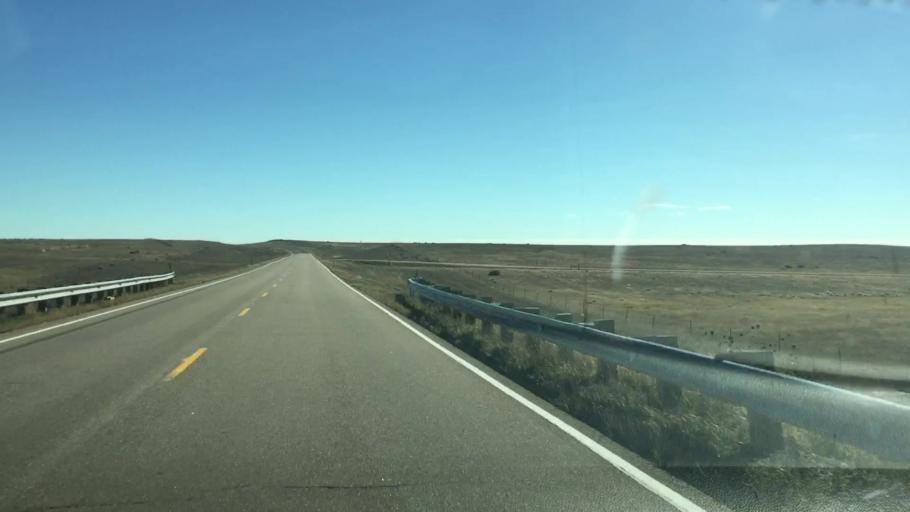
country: US
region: Colorado
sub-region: Lincoln County
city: Limon
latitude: 39.2957
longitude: -103.8642
